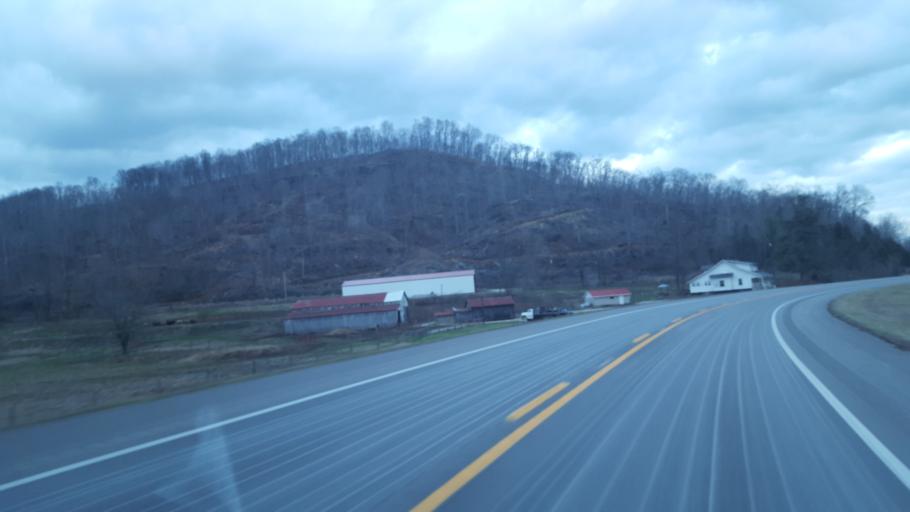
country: US
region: Kentucky
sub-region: Lewis County
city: Vanceburg
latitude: 38.5867
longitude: -83.4089
